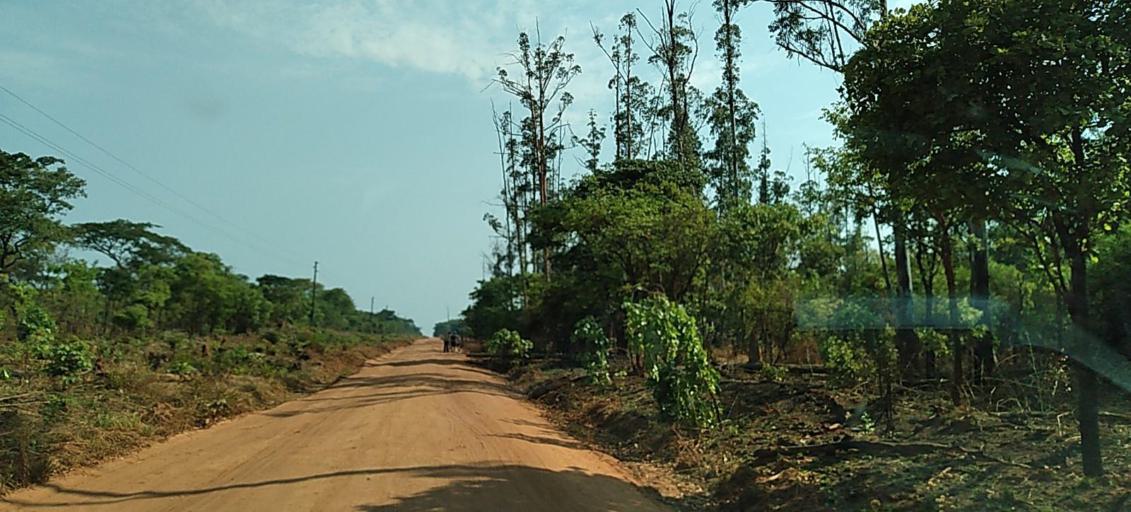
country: ZM
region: Copperbelt
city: Kalulushi
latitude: -12.9973
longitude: 27.8141
